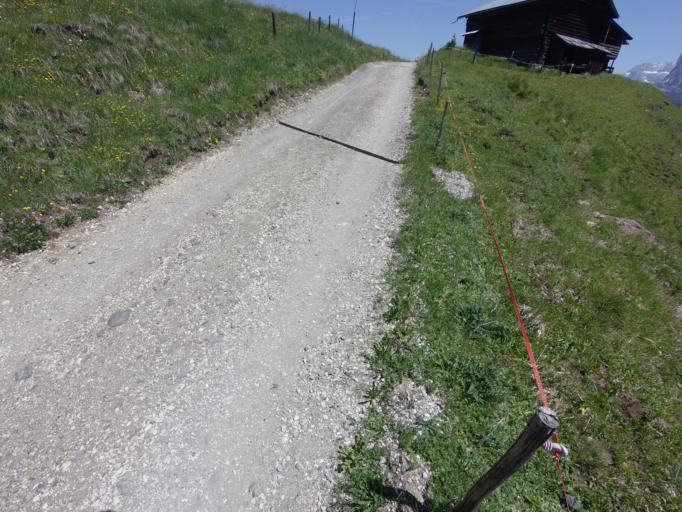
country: IT
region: Trentino-Alto Adige
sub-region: Bolzano
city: Ortisei
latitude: 46.5333
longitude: 11.6481
